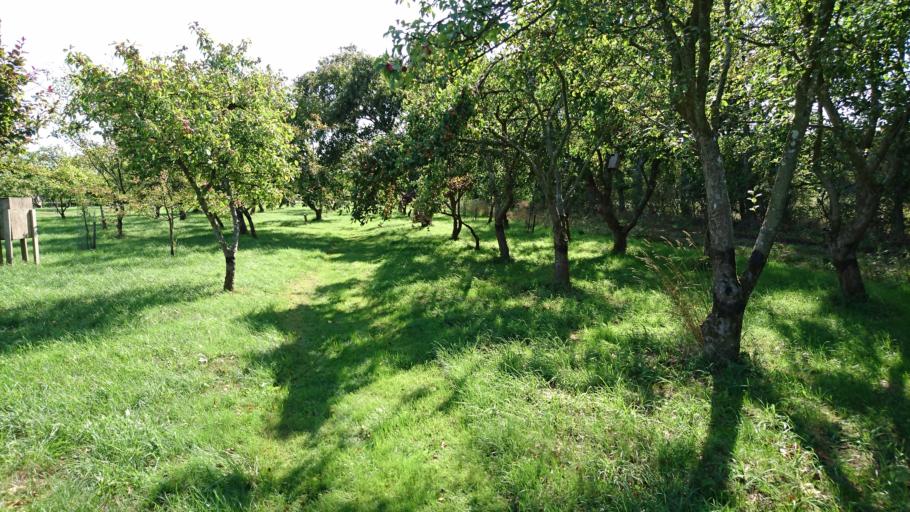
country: DK
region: North Denmark
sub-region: Frederikshavn Kommune
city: Saeby
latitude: 57.3441
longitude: 10.5045
